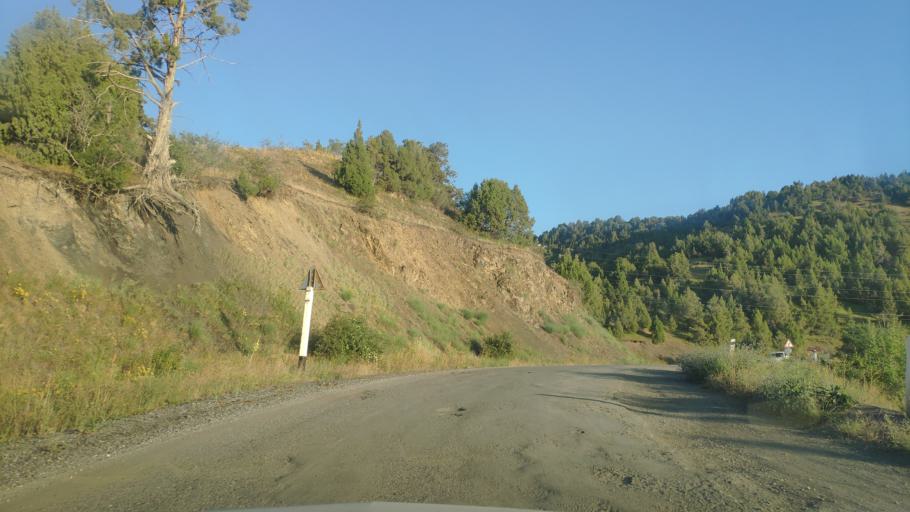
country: TJ
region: Viloyati Sughd
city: Ayni
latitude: 39.6411
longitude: 68.4698
